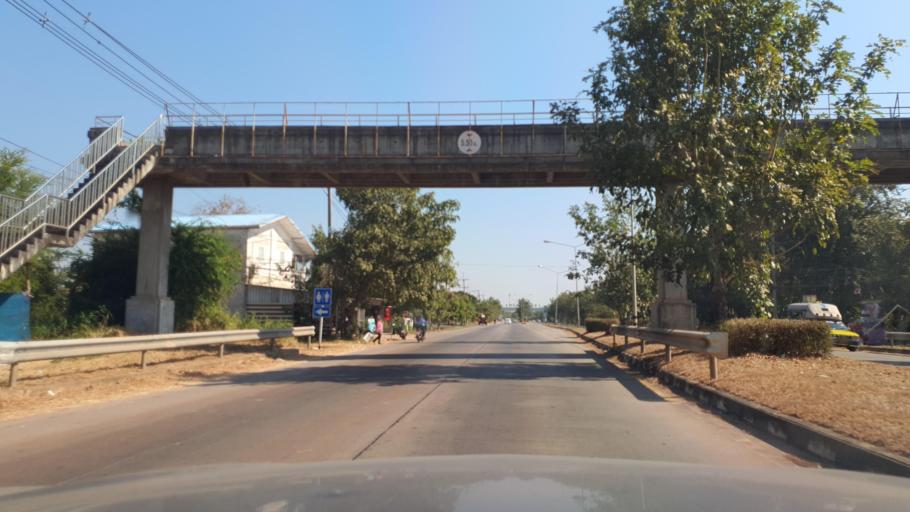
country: TH
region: Khon Kaen
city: Khon Kaen
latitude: 16.4323
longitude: 102.8922
